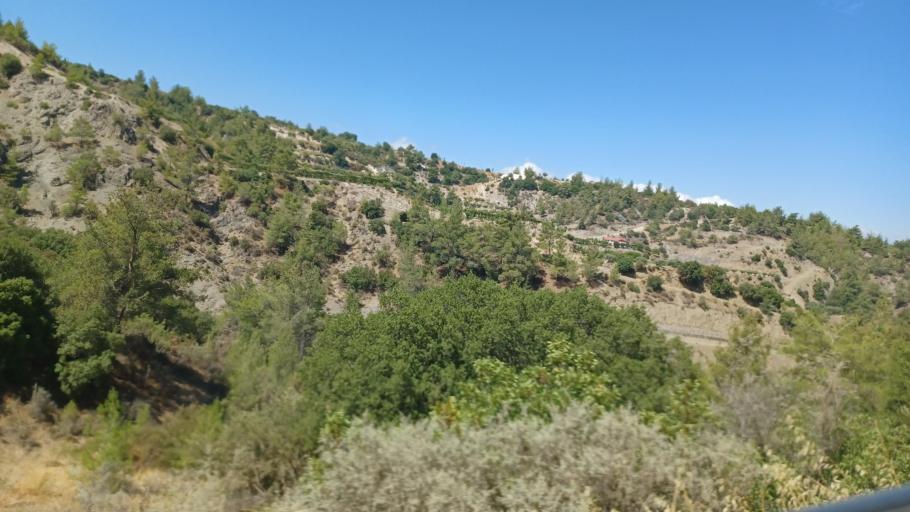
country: CY
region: Pafos
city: Mesogi
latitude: 34.9279
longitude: 32.6298
